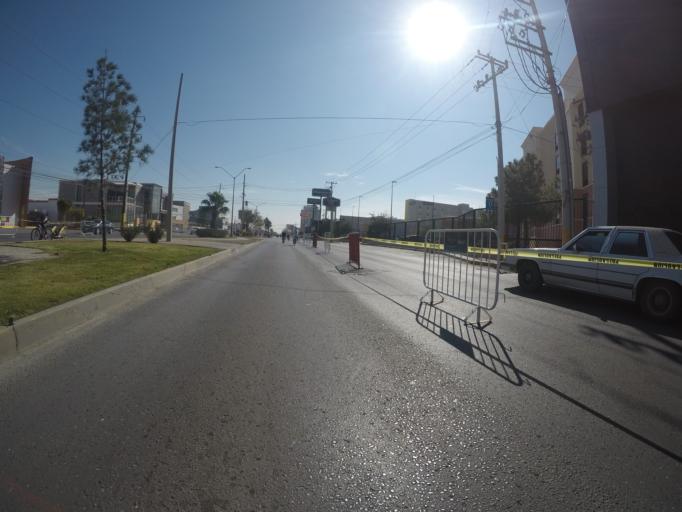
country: MX
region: Chihuahua
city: Ciudad Juarez
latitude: 31.7313
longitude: -106.4114
